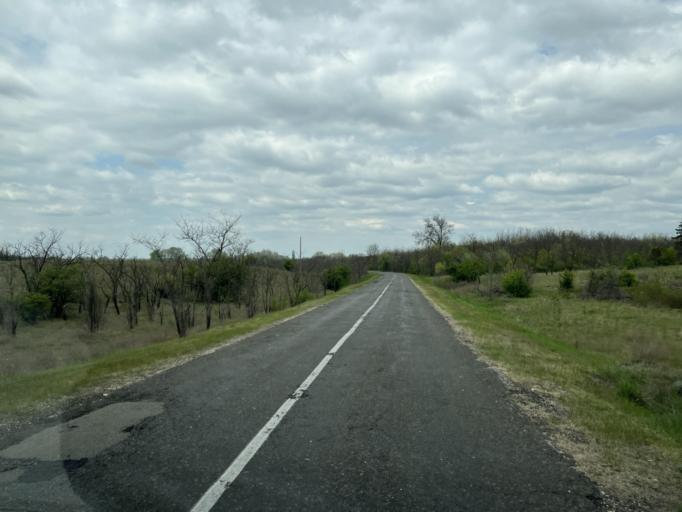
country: HU
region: Pest
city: Dabas
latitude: 47.1244
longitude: 19.3505
